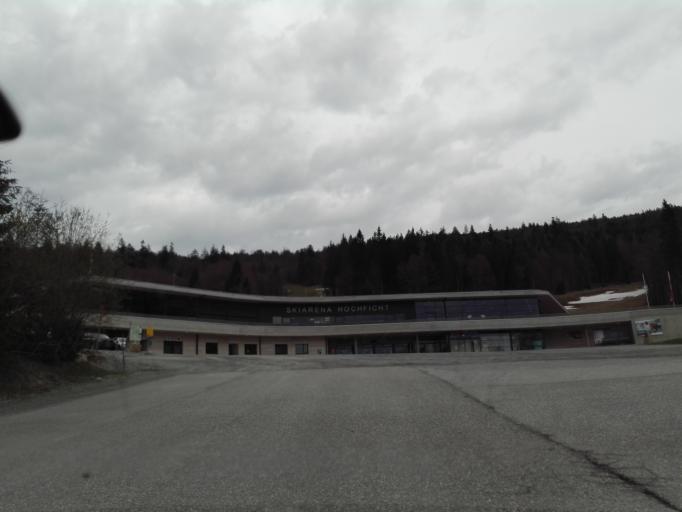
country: AT
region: Upper Austria
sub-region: Politischer Bezirk Rohrbach
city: Ulrichsberg
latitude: 48.7370
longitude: 13.8991
